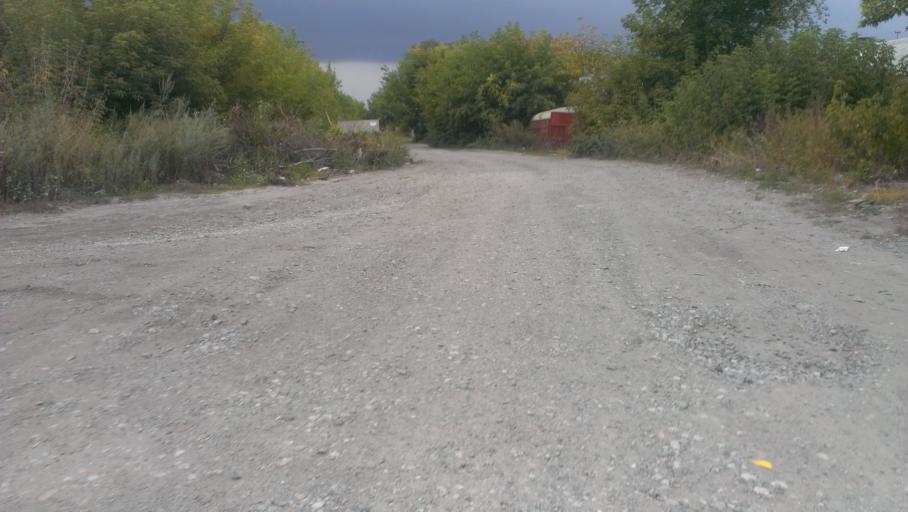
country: RU
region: Altai Krai
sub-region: Gorod Barnaulskiy
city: Barnaul
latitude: 53.3500
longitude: 83.7529
